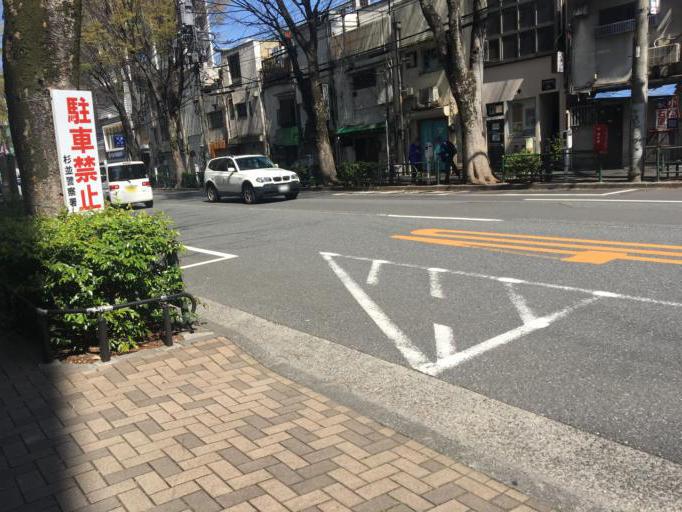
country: JP
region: Tokyo
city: Tokyo
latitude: 35.7021
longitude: 139.6361
